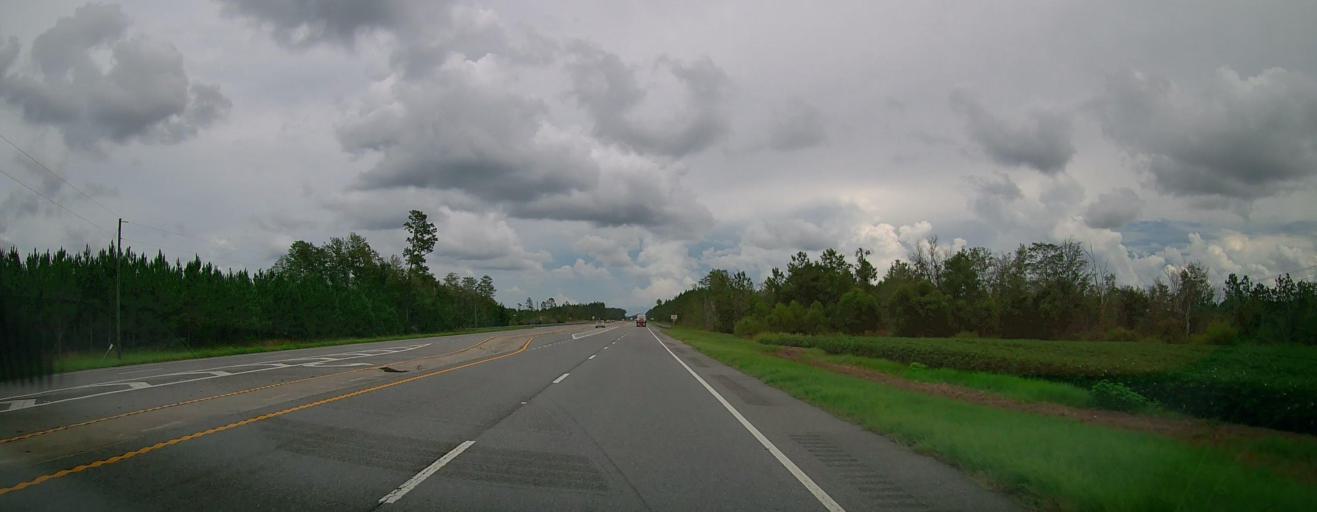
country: US
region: Georgia
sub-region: Wayne County
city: Jesup
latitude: 31.6756
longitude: -82.0740
